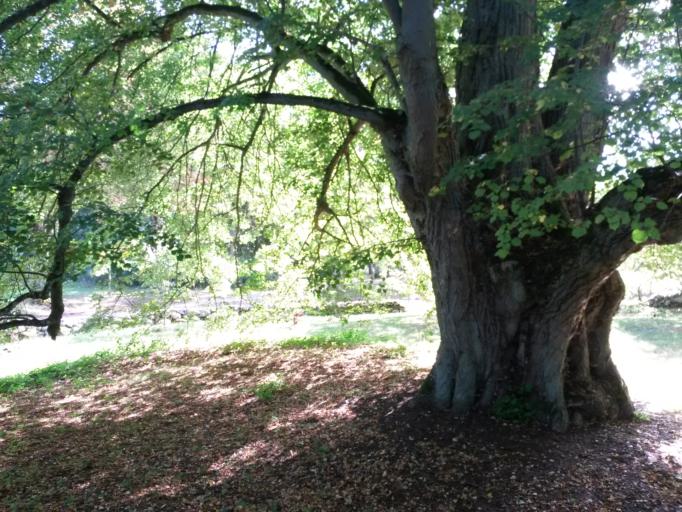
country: DE
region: Brandenburg
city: Lychen
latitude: 53.1595
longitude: 13.4054
